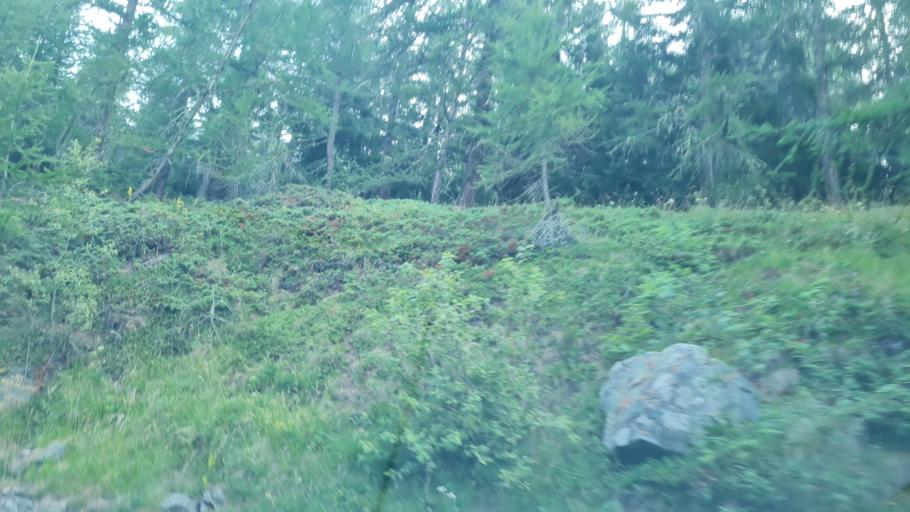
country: IT
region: Aosta Valley
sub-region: Valle d'Aosta
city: La Magdeleine
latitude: 45.8168
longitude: 7.6080
